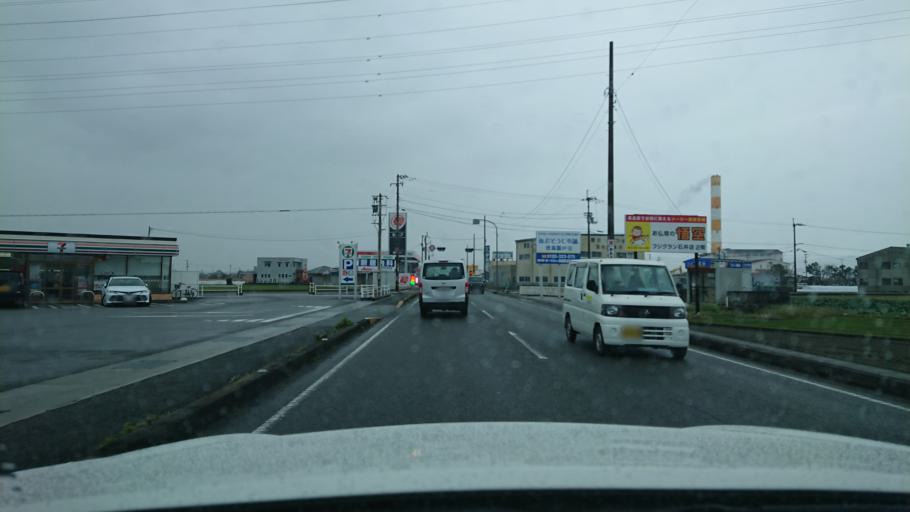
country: JP
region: Tokushima
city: Ishii
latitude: 34.0842
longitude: 134.4974
